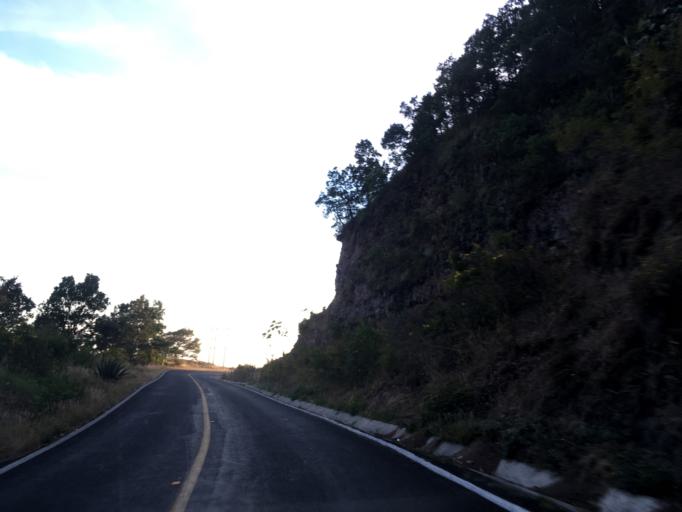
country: MX
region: Michoacan
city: Tzitzio
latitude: 19.6555
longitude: -100.9294
